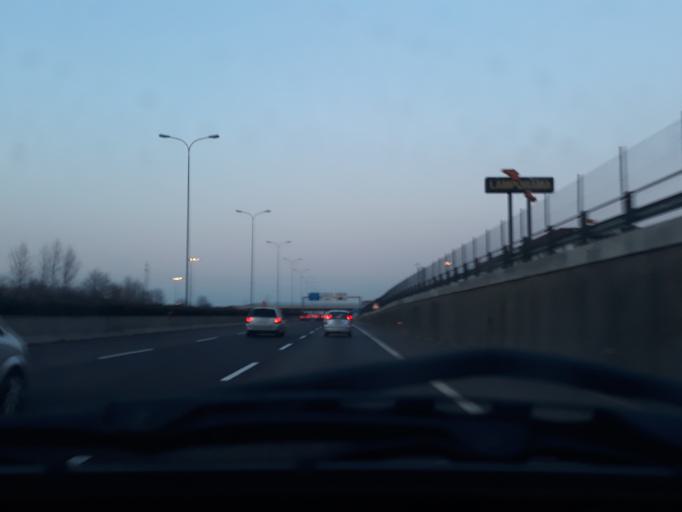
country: IT
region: Lombardy
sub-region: Provincia di Monza e Brianza
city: Santa Margherita
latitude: 45.6236
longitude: 9.2246
